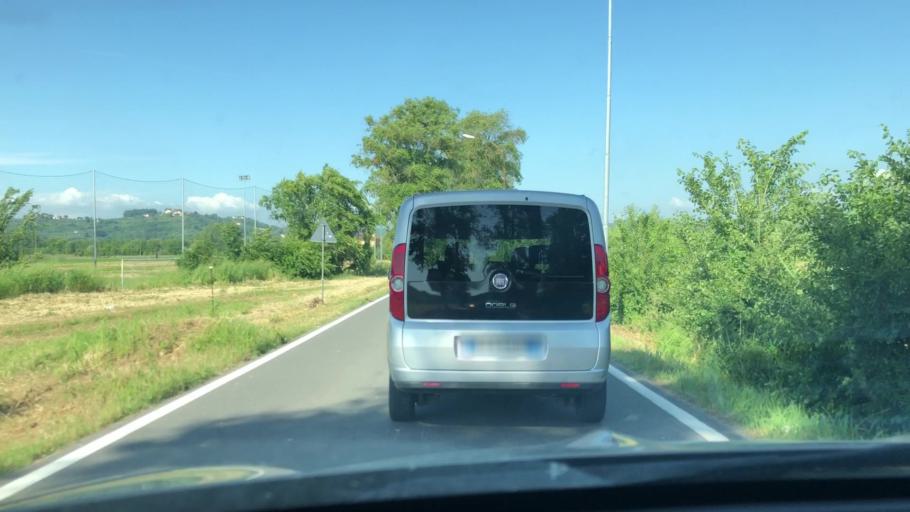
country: IT
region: Tuscany
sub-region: Province of Pisa
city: Capannoli
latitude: 43.5881
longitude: 10.6769
